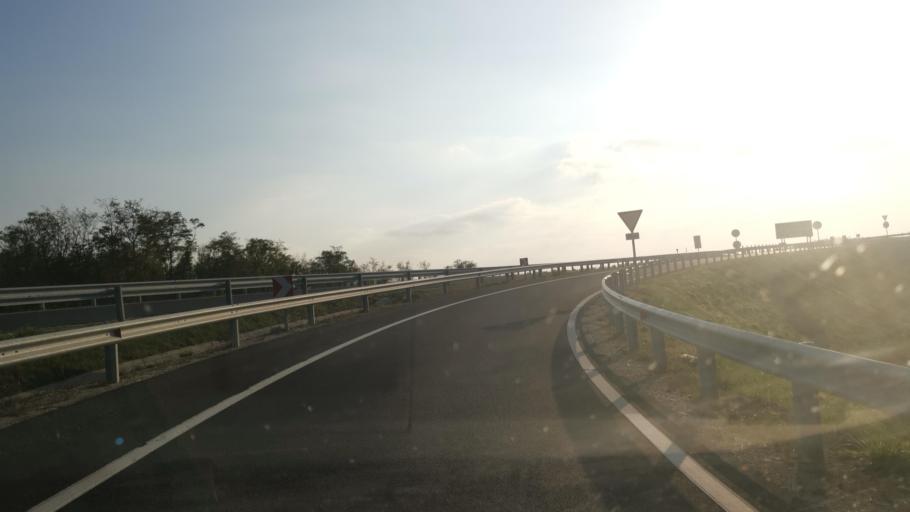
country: HU
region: Gyor-Moson-Sopron
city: Fertoszentmiklos
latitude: 47.5854
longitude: 16.9369
